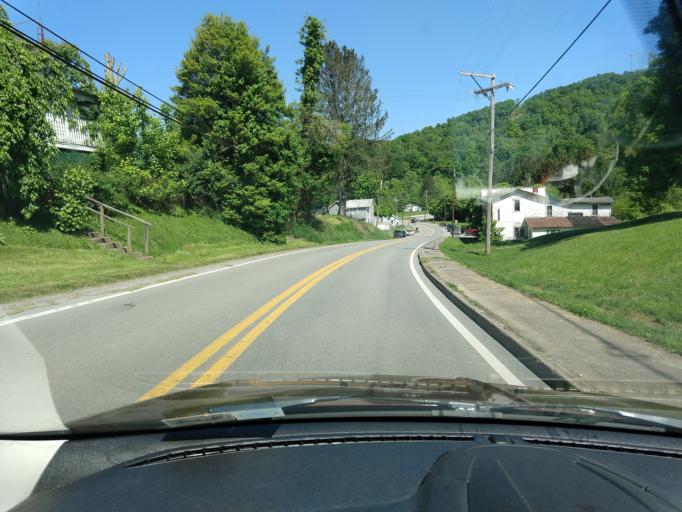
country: US
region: West Virginia
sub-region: Gilmer County
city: Glenville
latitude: 38.9132
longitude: -80.7487
